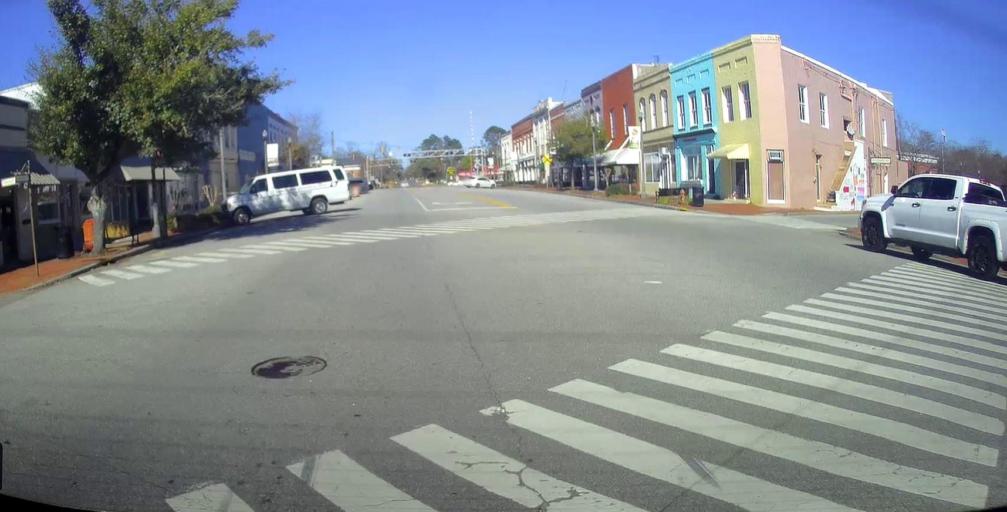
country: US
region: Georgia
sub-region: Macon County
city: Montezuma
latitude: 32.2995
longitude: -84.0306
